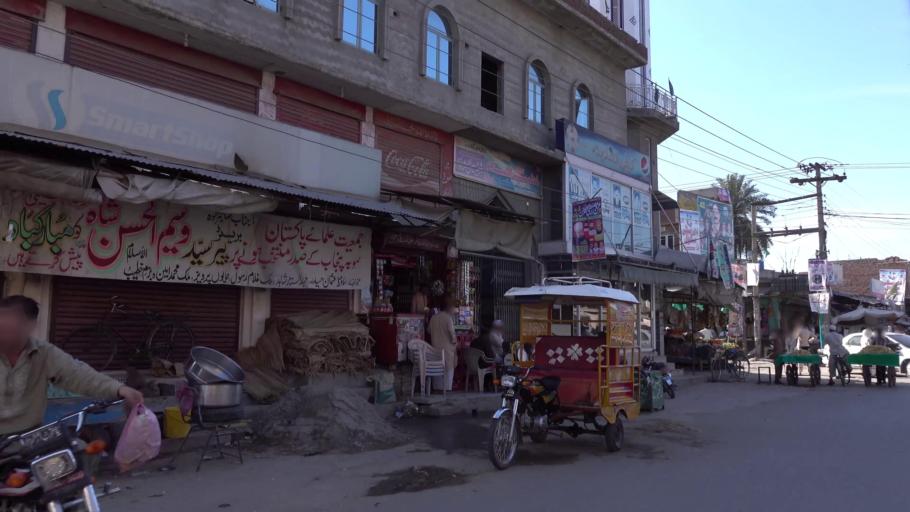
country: PK
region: Punjab
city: Hafizabad
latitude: 32.0756
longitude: 73.6847
